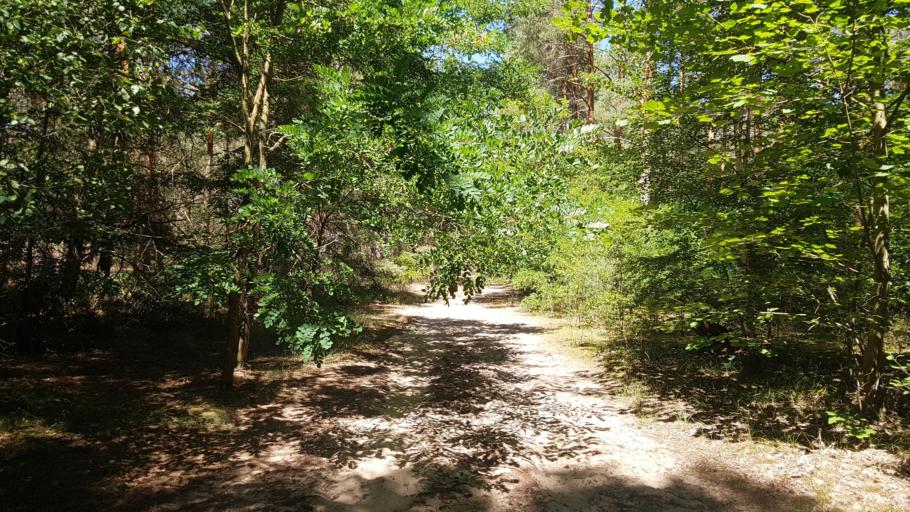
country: DE
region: Brandenburg
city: Trebbin
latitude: 52.2446
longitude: 13.1678
